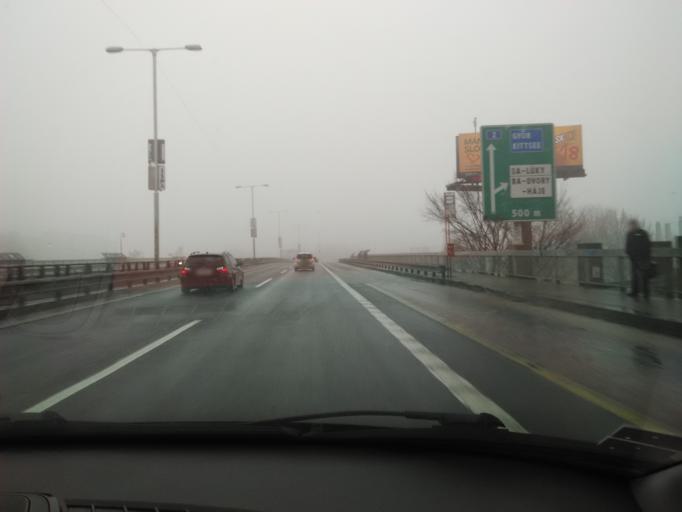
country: SK
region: Bratislavsky
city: Bratislava
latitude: 48.1284
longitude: 17.1049
